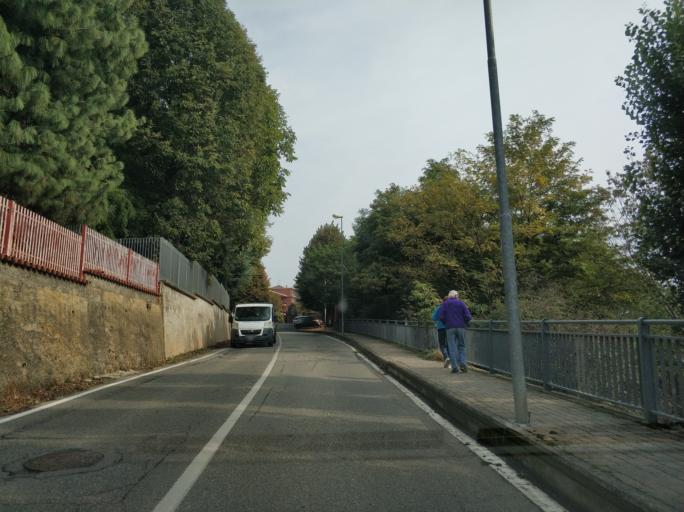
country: IT
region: Piedmont
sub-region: Provincia di Torino
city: San Carlo Canavese
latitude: 45.2423
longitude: 7.6103
